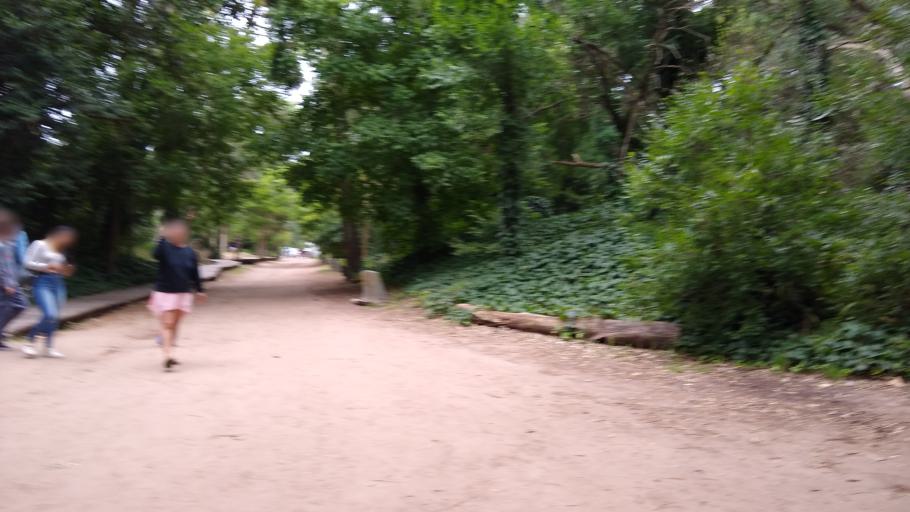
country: AR
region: Buenos Aires
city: Villa Gesell
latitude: -37.2505
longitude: -56.9640
